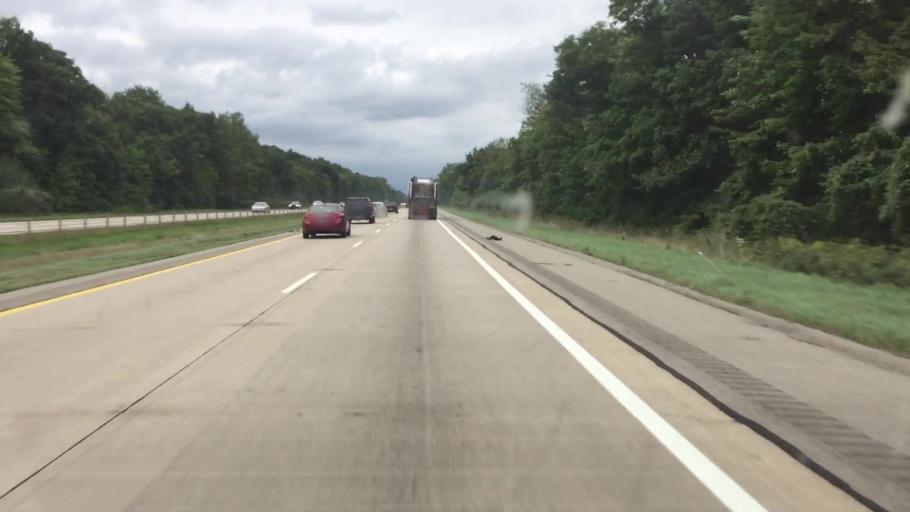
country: US
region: Michigan
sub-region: Monroe County
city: Petersburg
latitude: 41.8904
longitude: -83.6617
